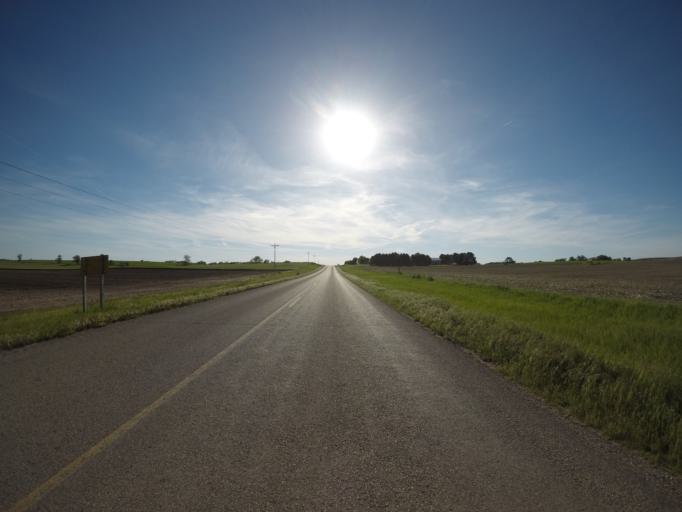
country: US
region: Kansas
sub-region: Clay County
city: Clay Center
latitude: 39.5243
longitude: -97.2024
